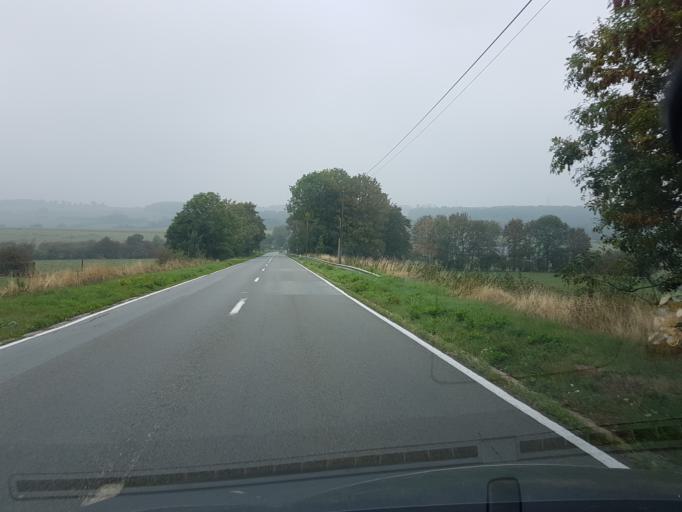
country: BE
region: Wallonia
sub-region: Province de Namur
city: Ohey
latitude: 50.4578
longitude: 5.1062
